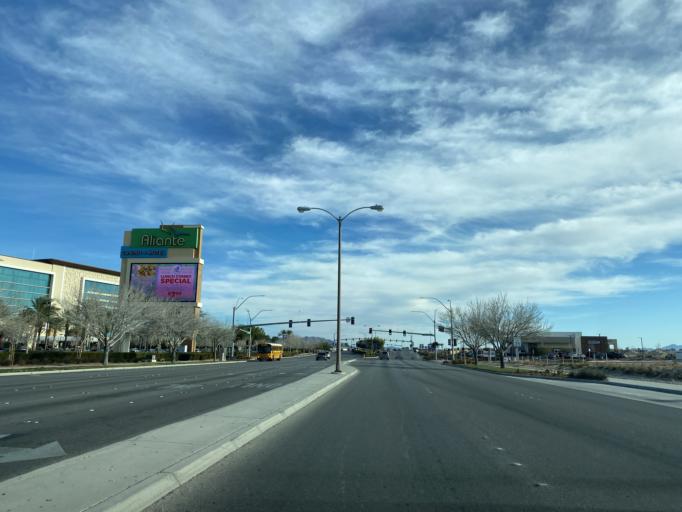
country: US
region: Nevada
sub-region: Clark County
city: North Las Vegas
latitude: 36.2923
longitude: -115.1836
